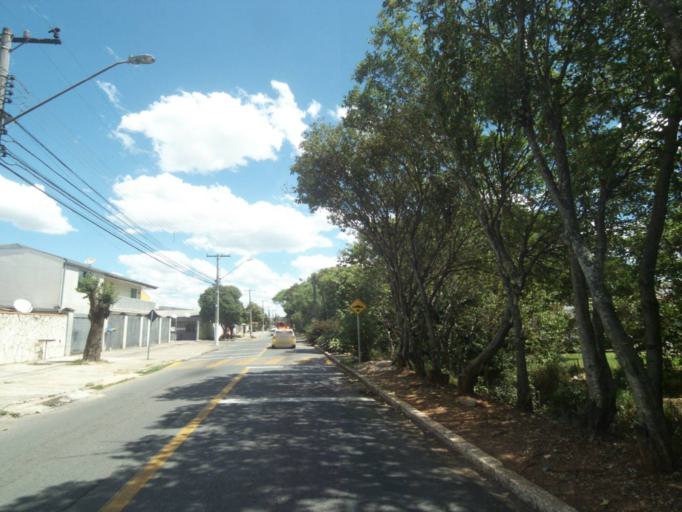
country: BR
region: Parana
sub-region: Curitiba
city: Curitiba
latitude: -25.5049
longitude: -49.3264
